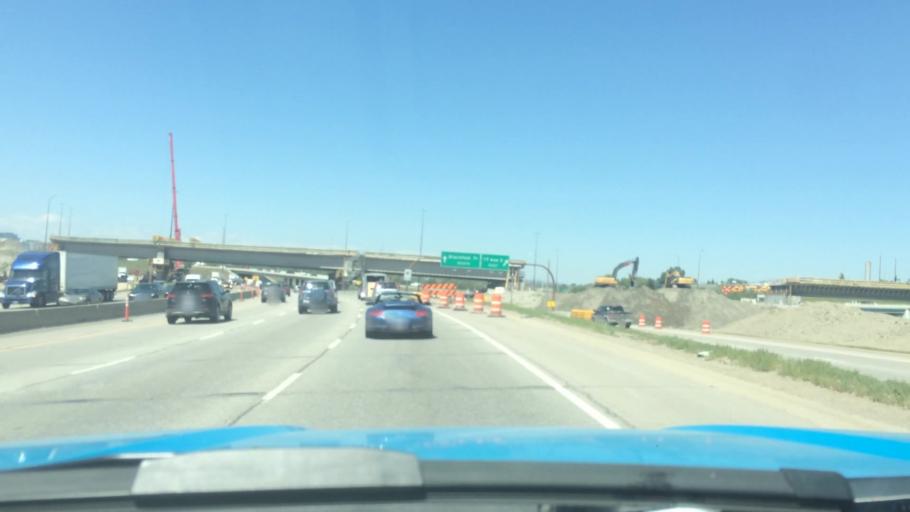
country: CA
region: Alberta
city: Calgary
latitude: 51.0345
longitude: -113.9996
